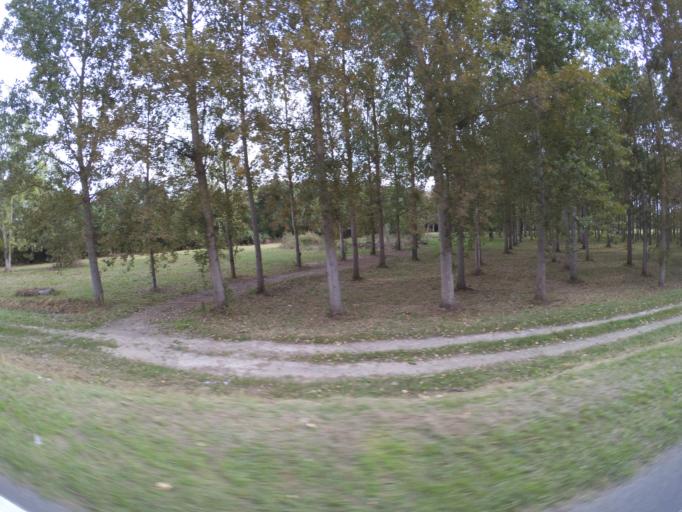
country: FR
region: Centre
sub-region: Departement d'Indre-et-Loire
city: Vernou-sur-Brenne
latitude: 47.4290
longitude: 0.8493
